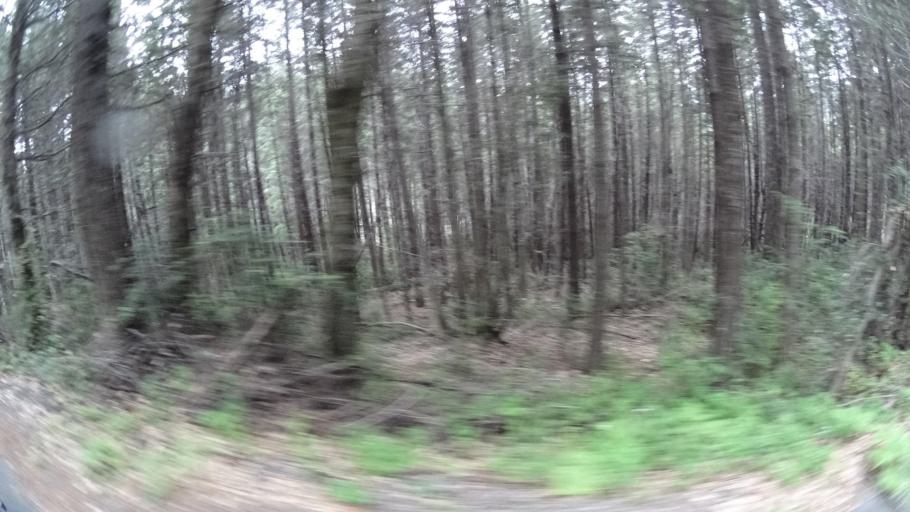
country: US
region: California
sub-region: Humboldt County
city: Willow Creek
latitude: 41.1993
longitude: -123.7593
